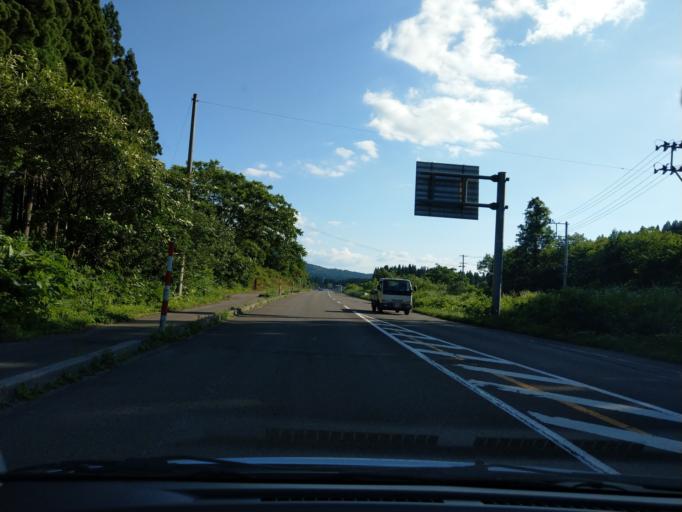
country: JP
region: Akita
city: Takanosu
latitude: 40.1403
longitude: 140.3863
